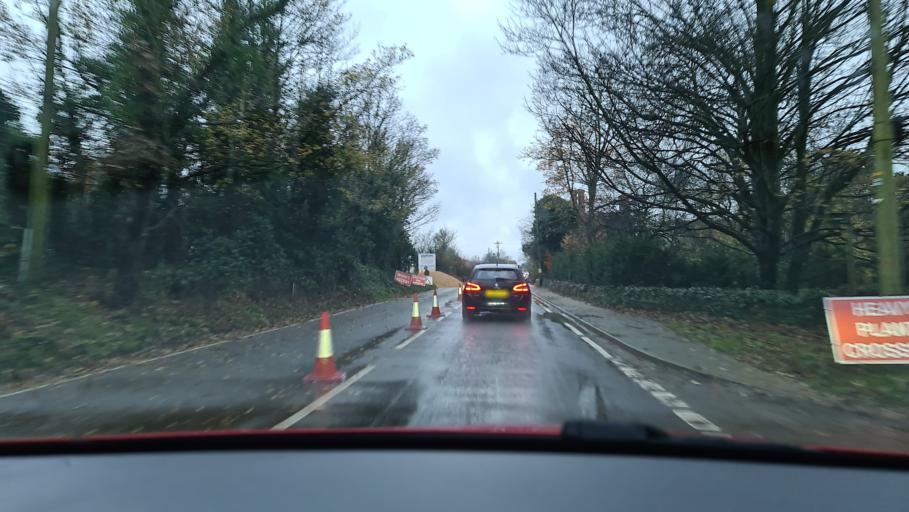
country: GB
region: England
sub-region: Oxfordshire
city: Somerton
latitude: 51.9418
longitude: -1.2120
